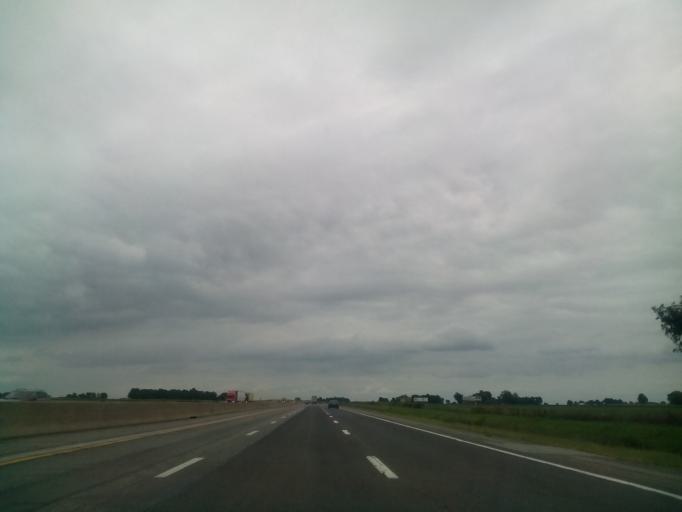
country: US
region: Ohio
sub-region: Huron County
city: Monroeville
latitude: 41.3377
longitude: -82.7395
